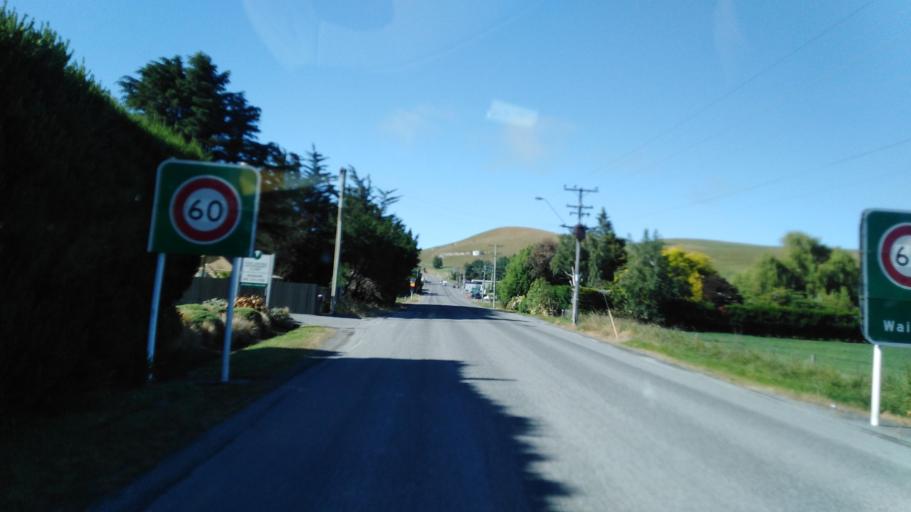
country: NZ
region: Canterbury
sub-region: Hurunui District
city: Amberley
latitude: -42.9674
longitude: 172.7065
